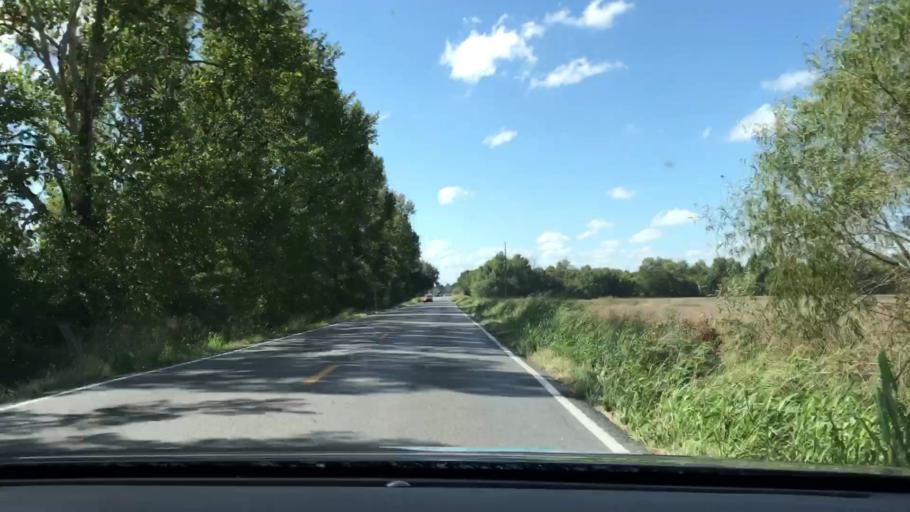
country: US
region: Kentucky
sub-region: Graves County
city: Mayfield
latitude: 36.7511
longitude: -88.6139
